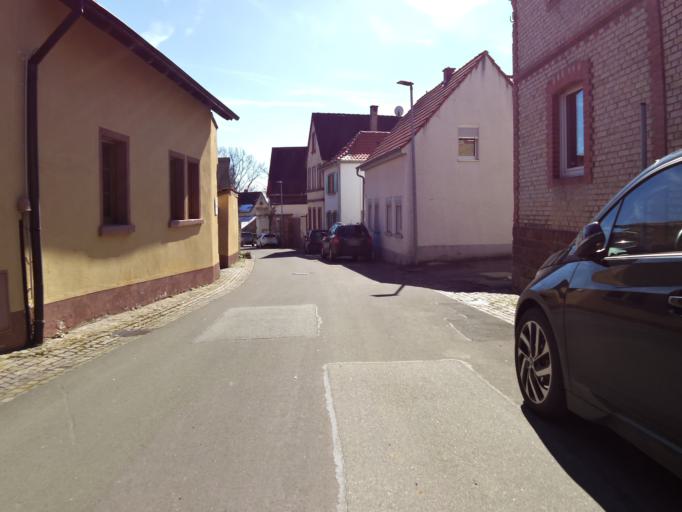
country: DE
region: Rheinland-Pfalz
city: Heidesheim
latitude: 49.5860
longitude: 8.1850
